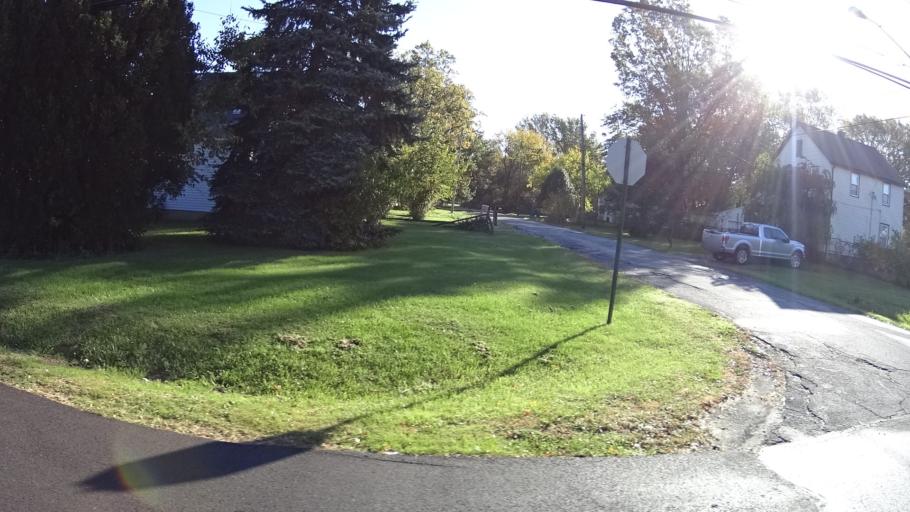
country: US
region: Ohio
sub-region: Lorain County
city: Lorain
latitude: 41.4332
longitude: -82.1575
